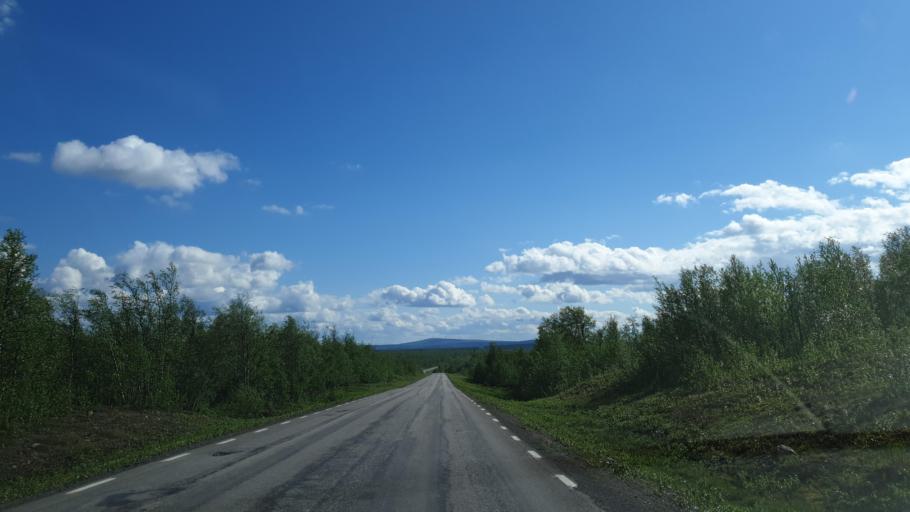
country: SE
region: Norrbotten
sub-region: Kiruna Kommun
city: Kiruna
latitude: 67.7925
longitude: 20.2311
